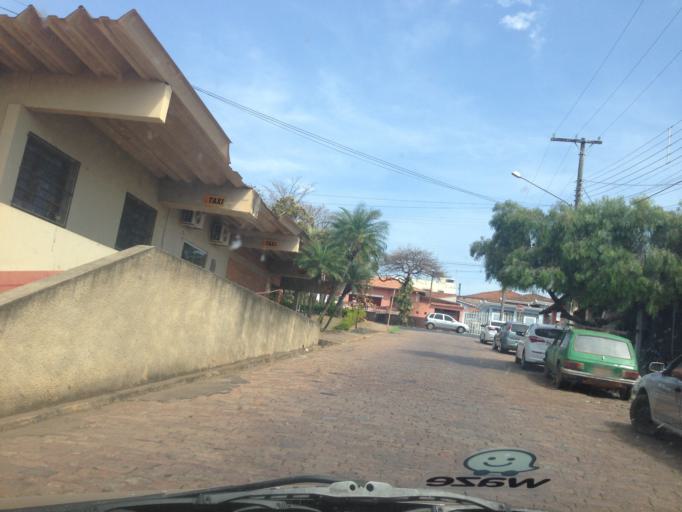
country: BR
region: Sao Paulo
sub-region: Casa Branca
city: Casa Branca
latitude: -21.7779
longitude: -47.0744
